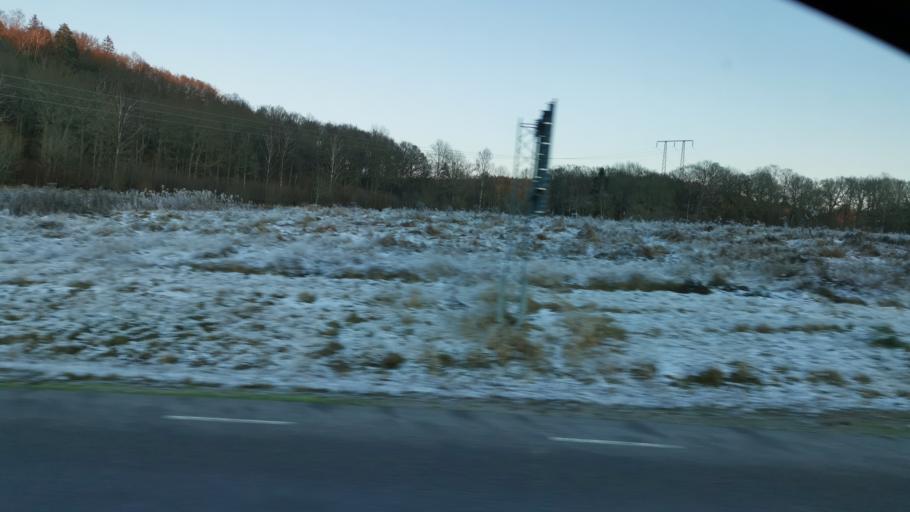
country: SE
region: Vaestra Goetaland
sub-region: Munkedals Kommun
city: Munkedal
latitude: 58.4468
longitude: 11.6964
